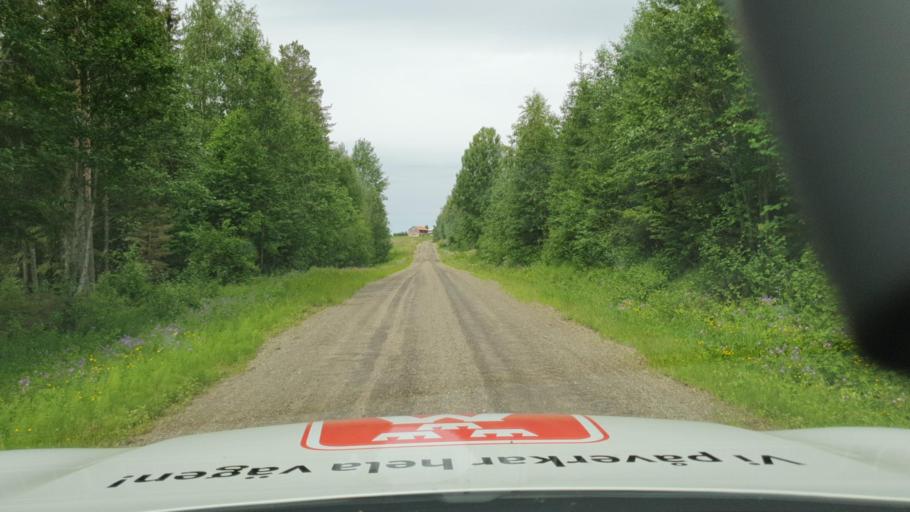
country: SE
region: Vaesterbotten
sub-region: Robertsfors Kommun
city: Robertsfors
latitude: 64.2777
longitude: 20.6871
